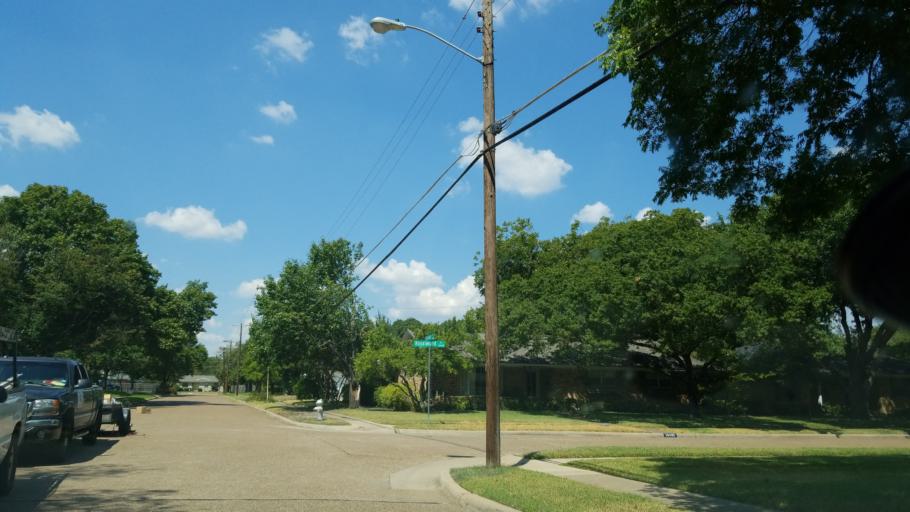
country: US
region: Texas
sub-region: Dallas County
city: Richardson
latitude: 32.8835
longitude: -96.7061
